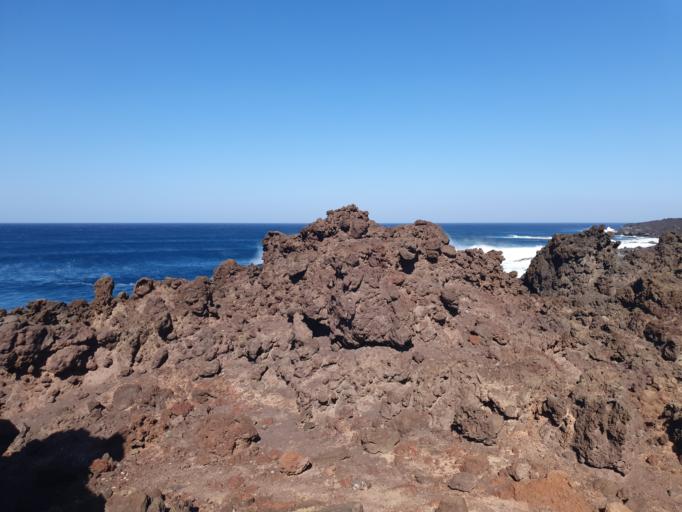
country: ES
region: Canary Islands
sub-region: Provincia de Las Palmas
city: Tinajo
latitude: 29.0666
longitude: -13.7612
